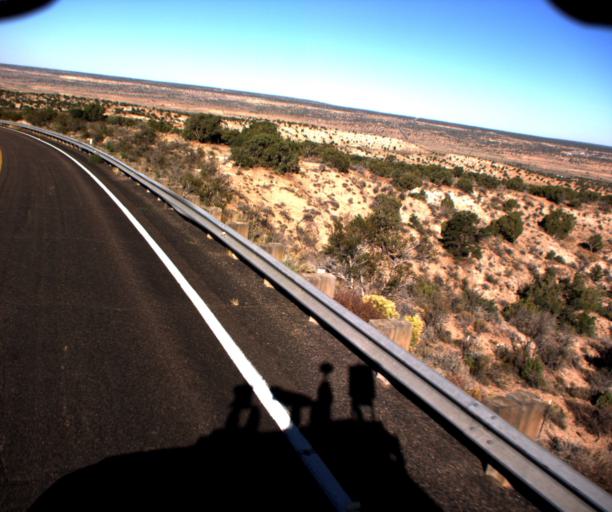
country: US
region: Arizona
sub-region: Navajo County
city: First Mesa
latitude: 35.7346
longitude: -110.1109
